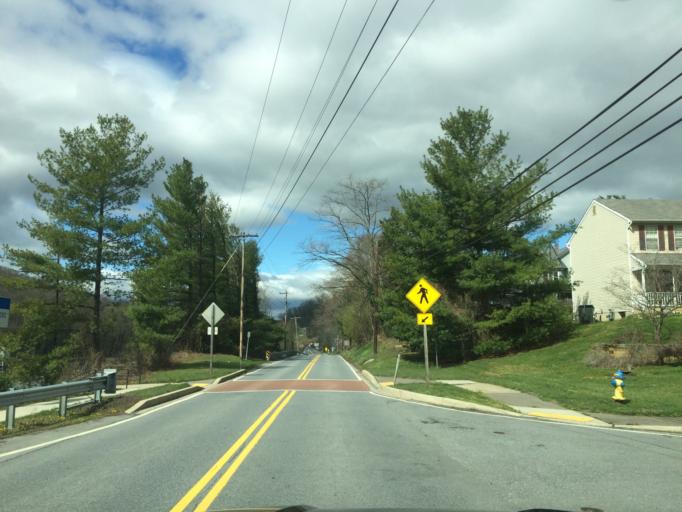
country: US
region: Maryland
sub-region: Frederick County
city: Point of Rocks
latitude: 39.2742
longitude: -77.5335
